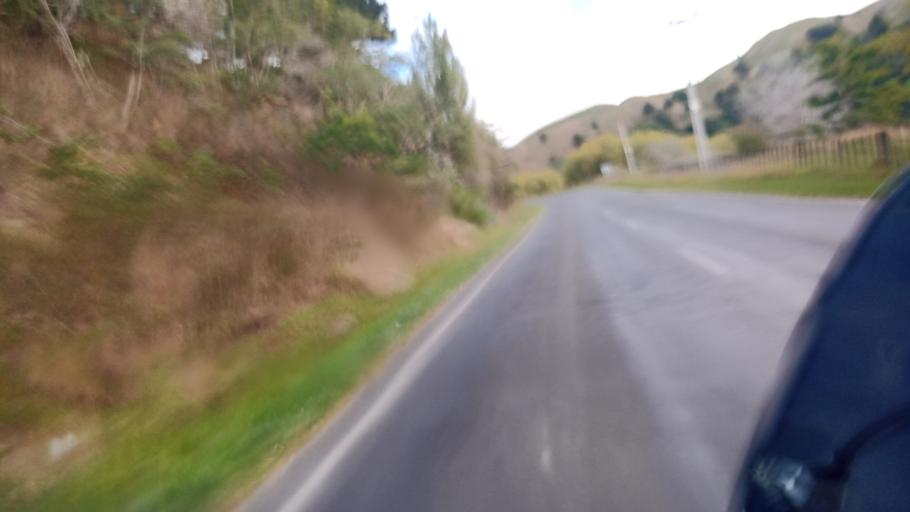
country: NZ
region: Gisborne
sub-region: Gisborne District
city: Gisborne
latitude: -38.5902
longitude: 177.7676
